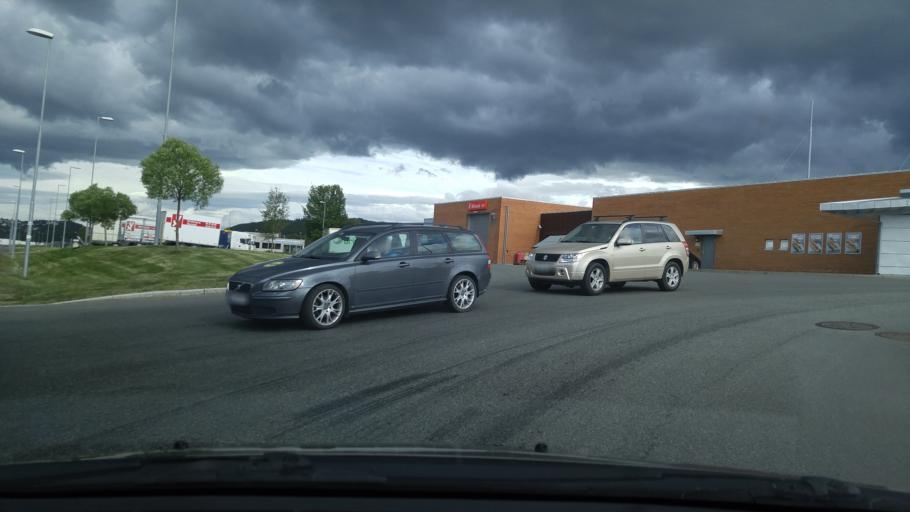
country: NO
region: Nord-Trondelag
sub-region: Levanger
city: Skogn
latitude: 63.7179
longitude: 11.2251
